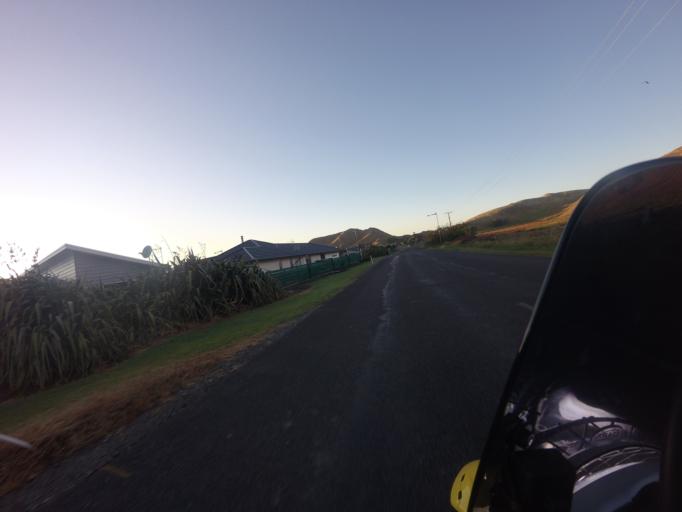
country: NZ
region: Gisborne
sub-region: Gisborne District
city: Gisborne
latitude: -38.6892
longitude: 178.0565
